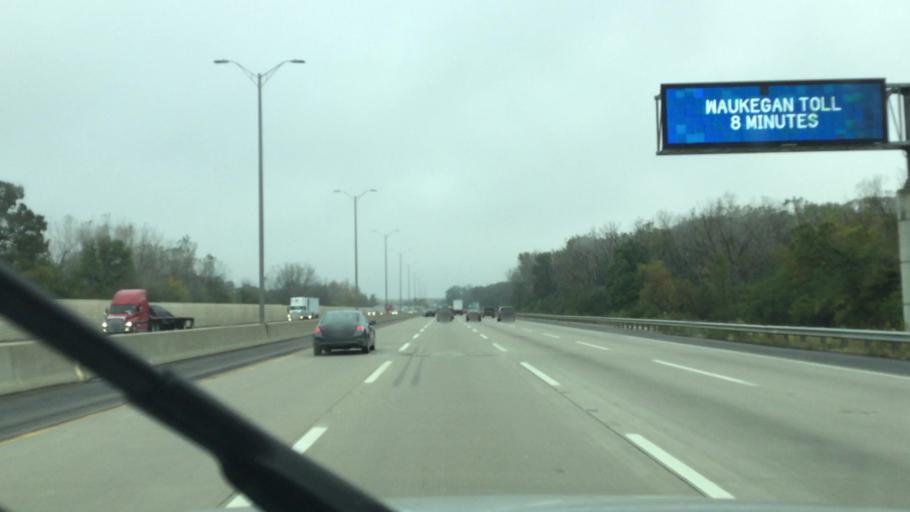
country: US
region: Illinois
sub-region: Lake County
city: Green Oaks
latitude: 42.3198
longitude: -87.9060
